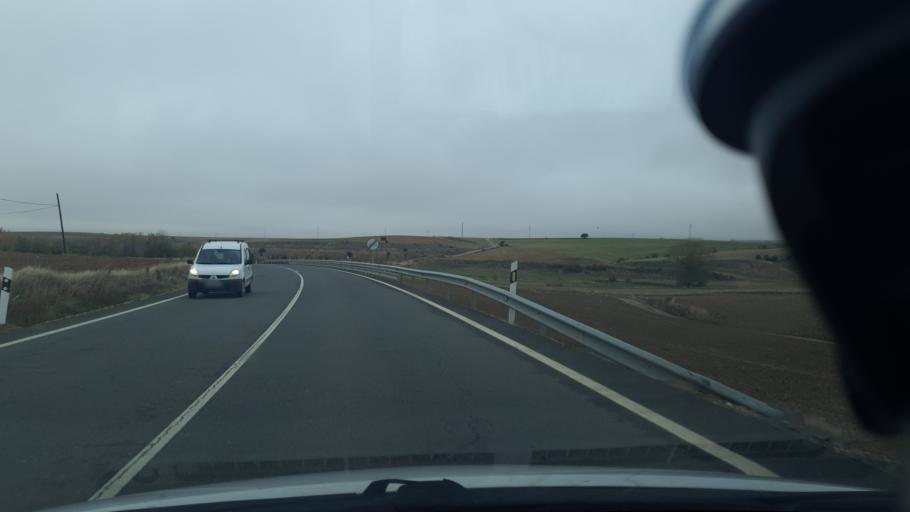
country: ES
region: Castille and Leon
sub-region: Provincia de Segovia
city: Encinillas
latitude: 41.0062
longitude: -4.1490
